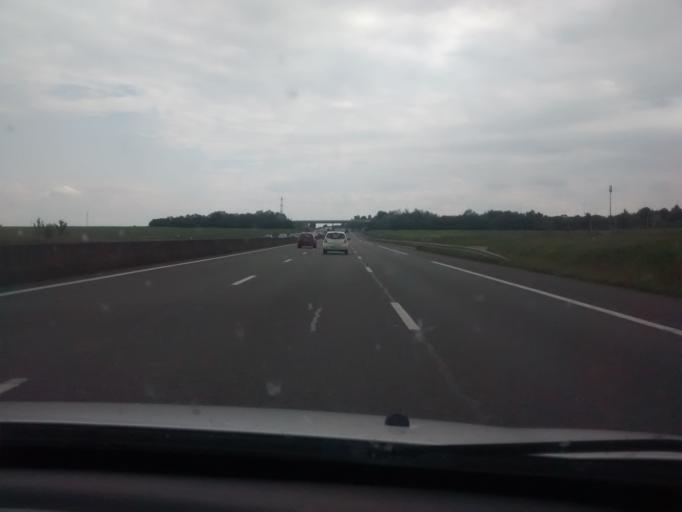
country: FR
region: Centre
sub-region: Departement d'Eure-et-Loir
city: Le Coudray
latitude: 48.4179
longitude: 1.5084
